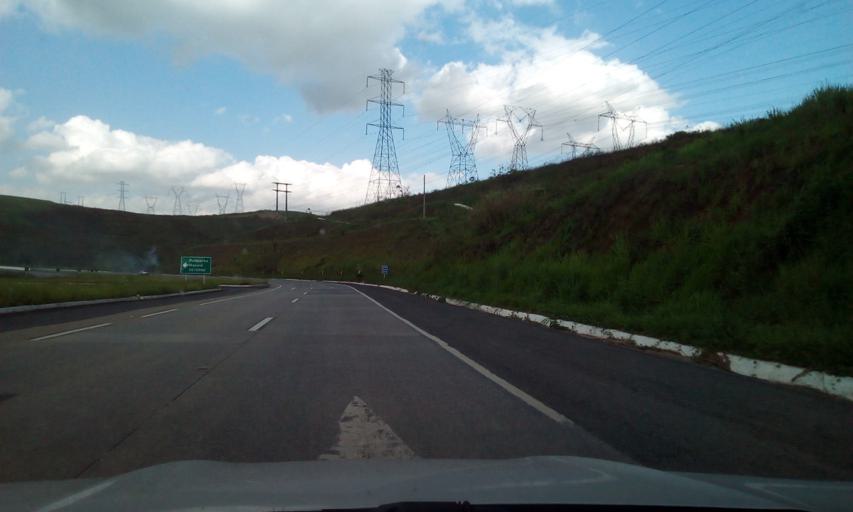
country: BR
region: Pernambuco
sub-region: Joaquim Nabuco
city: Joaquim Nabuco
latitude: -8.6205
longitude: -35.5488
